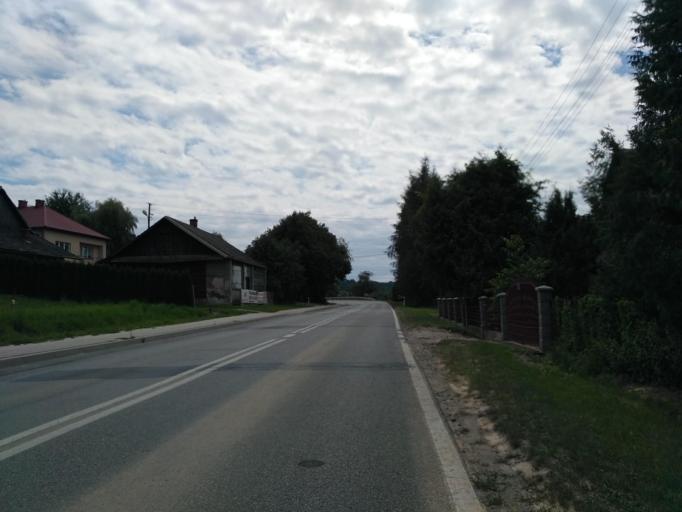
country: PL
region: Subcarpathian Voivodeship
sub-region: Powiat rzeszowski
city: Chmielnik
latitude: 49.9471
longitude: 22.1009
